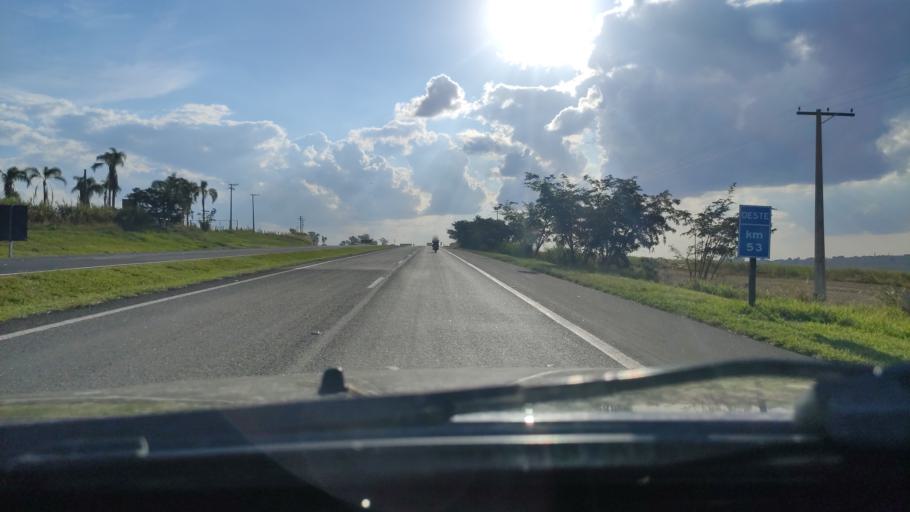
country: BR
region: Sao Paulo
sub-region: Mogi-Mirim
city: Mogi Mirim
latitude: -22.4561
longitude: -46.9129
